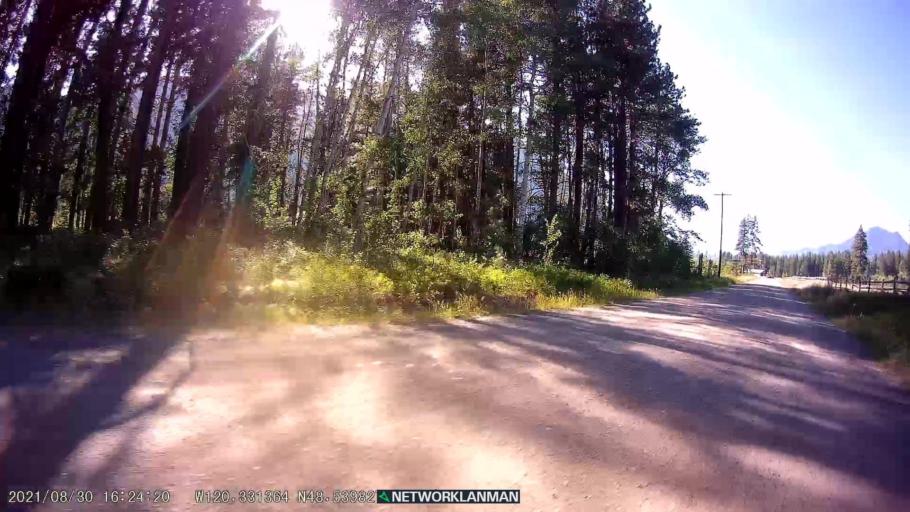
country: US
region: Washington
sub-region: Chelan County
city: Granite Falls
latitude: 48.5402
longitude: -120.3296
